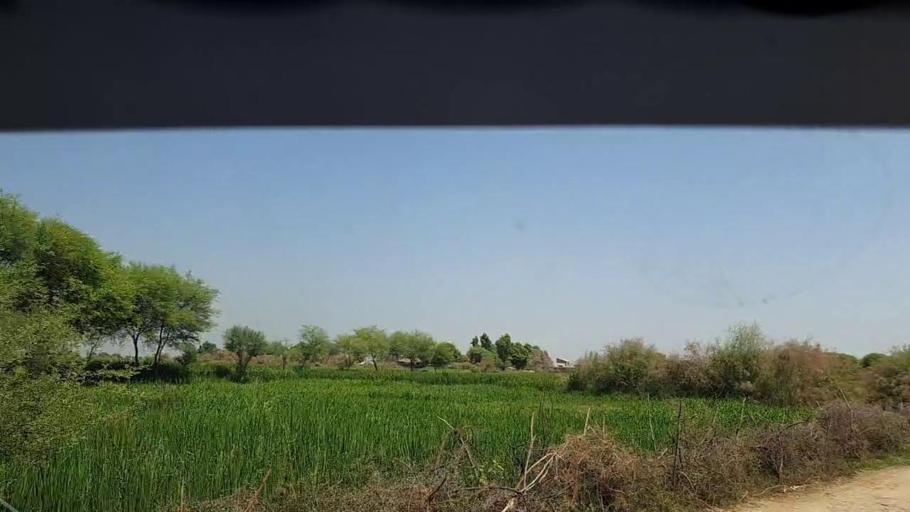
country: PK
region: Sindh
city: Ghauspur
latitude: 28.1627
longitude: 69.1405
